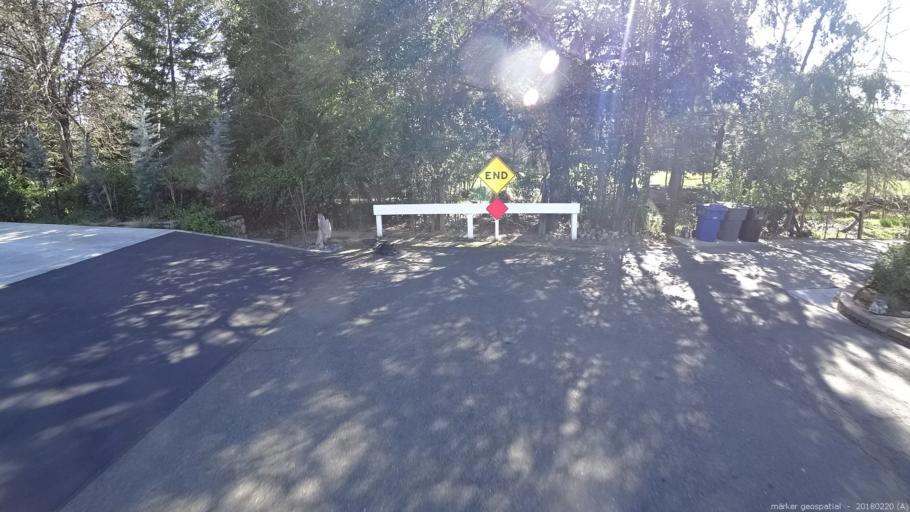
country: US
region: California
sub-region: Sacramento County
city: Orangevale
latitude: 38.6990
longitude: -121.2031
